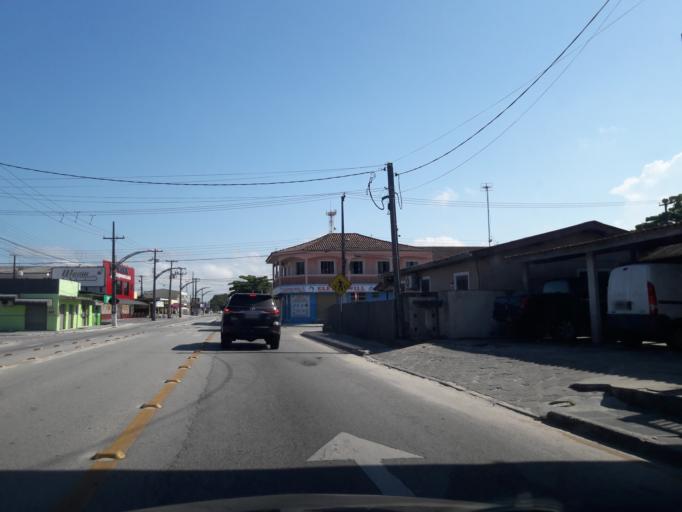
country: BR
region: Parana
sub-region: Pontal Do Parana
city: Pontal do Parana
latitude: -25.6946
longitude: -48.4745
